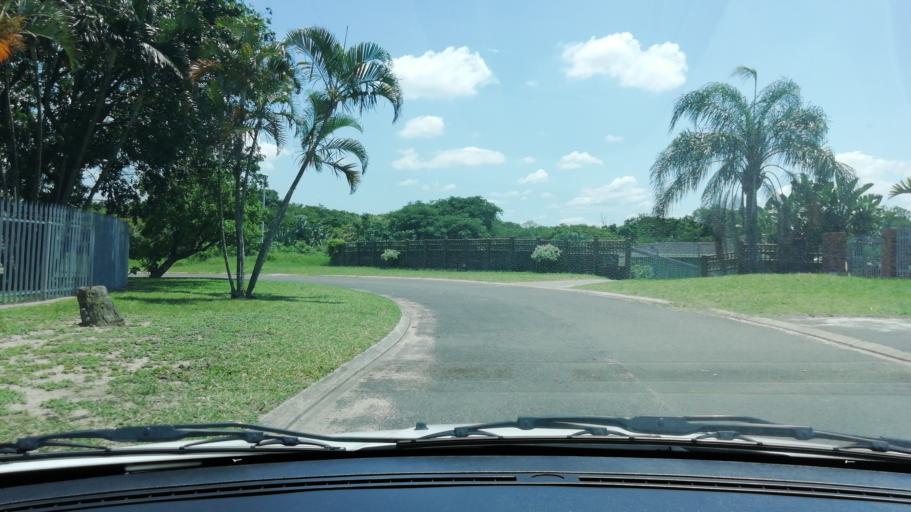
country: ZA
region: KwaZulu-Natal
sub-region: uThungulu District Municipality
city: Richards Bay
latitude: -28.7332
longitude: 32.0536
